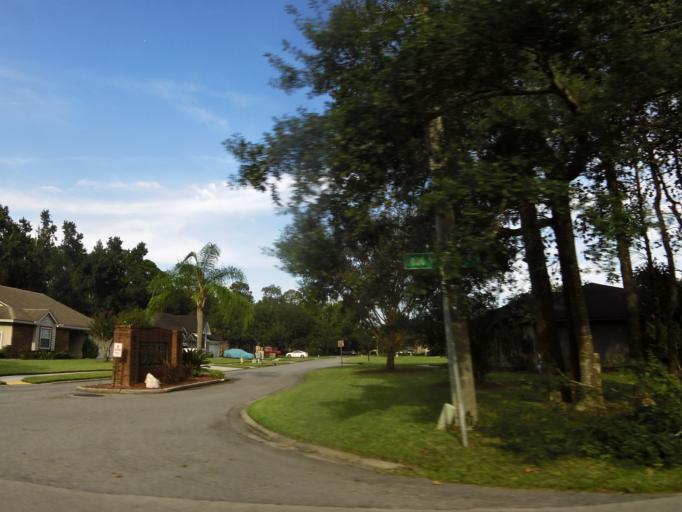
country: US
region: Florida
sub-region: Saint Johns County
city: Fruit Cove
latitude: 30.1461
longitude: -81.5956
